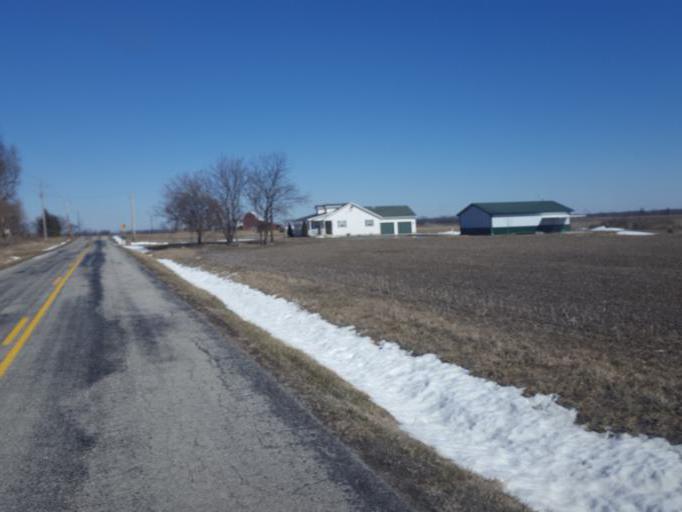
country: US
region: Ohio
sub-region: Wyandot County
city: Upper Sandusky
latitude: 40.6792
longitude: -83.2981
